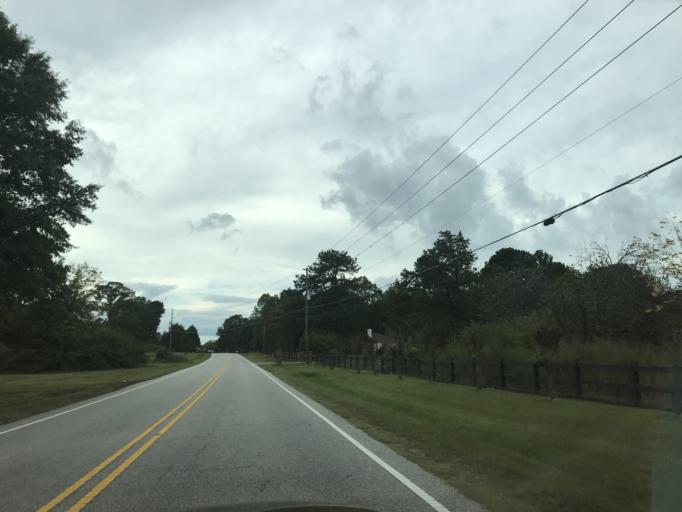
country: US
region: North Carolina
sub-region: Franklin County
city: Youngsville
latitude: 35.9865
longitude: -78.3963
